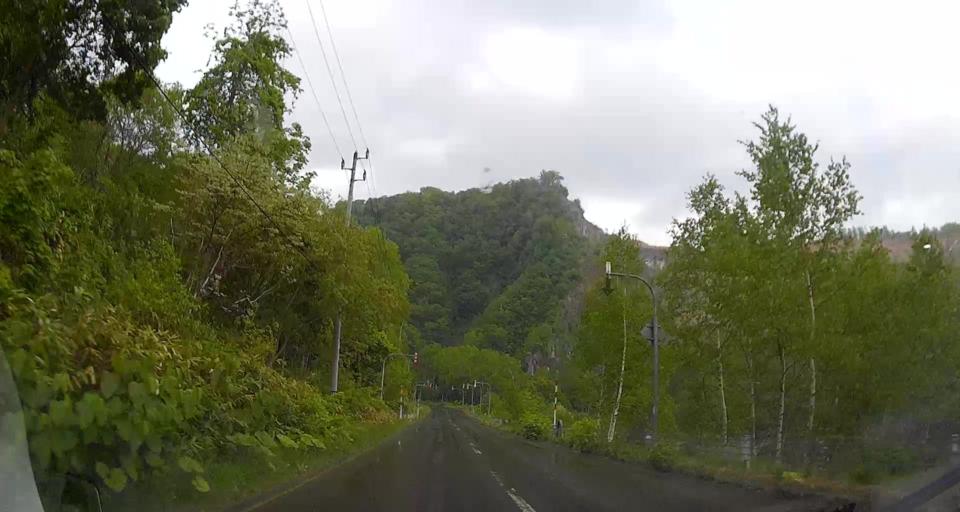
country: JP
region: Hokkaido
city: Niseko Town
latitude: 42.9017
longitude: 140.9117
